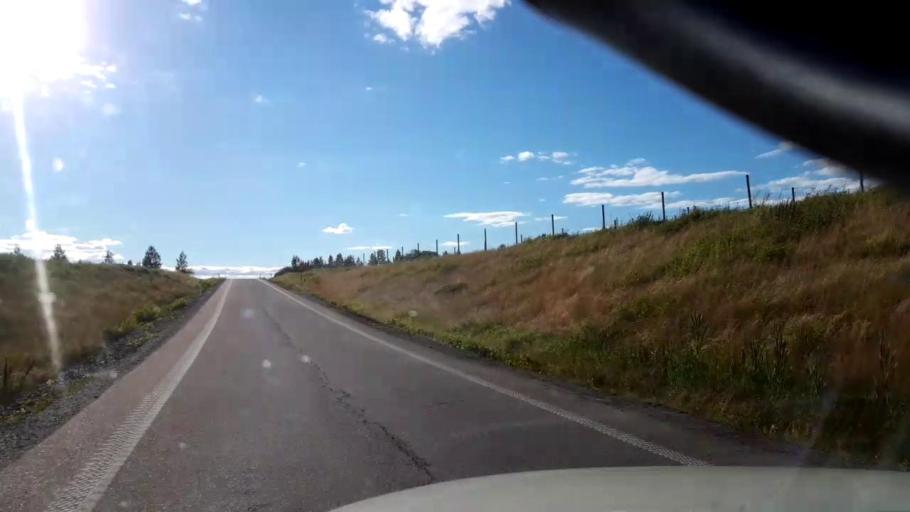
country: SE
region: Dalarna
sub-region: Borlange Kommun
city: Ornas
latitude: 60.4242
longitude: 15.5401
